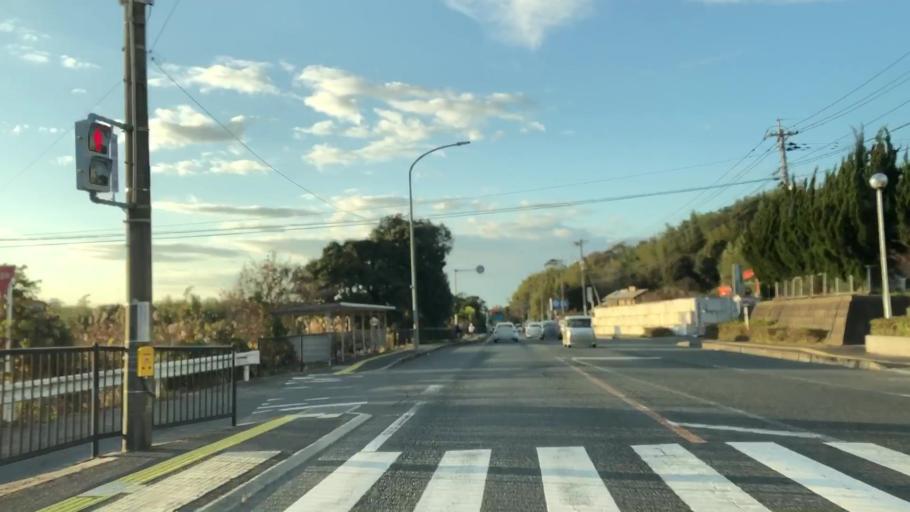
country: JP
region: Fukuoka
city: Nakatsu
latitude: 33.5367
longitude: 131.3024
